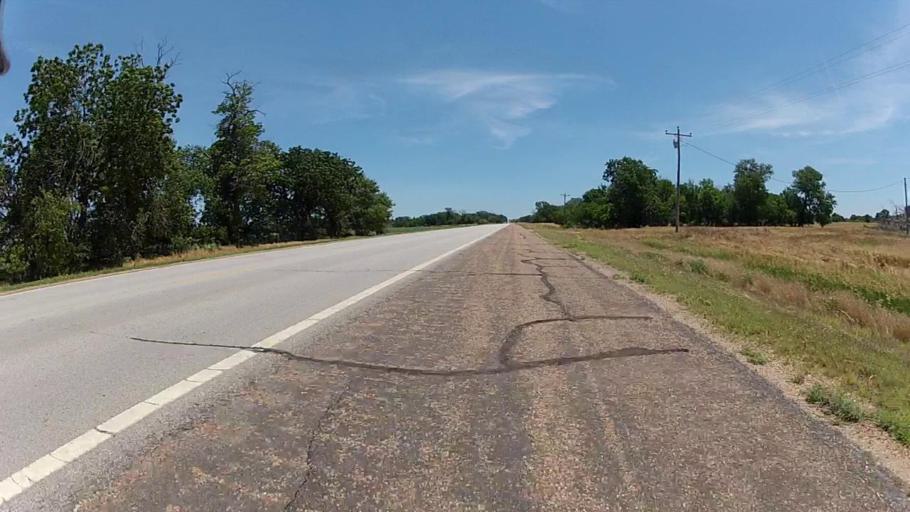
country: US
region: Kansas
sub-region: Barber County
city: Medicine Lodge
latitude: 37.2535
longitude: -98.3359
